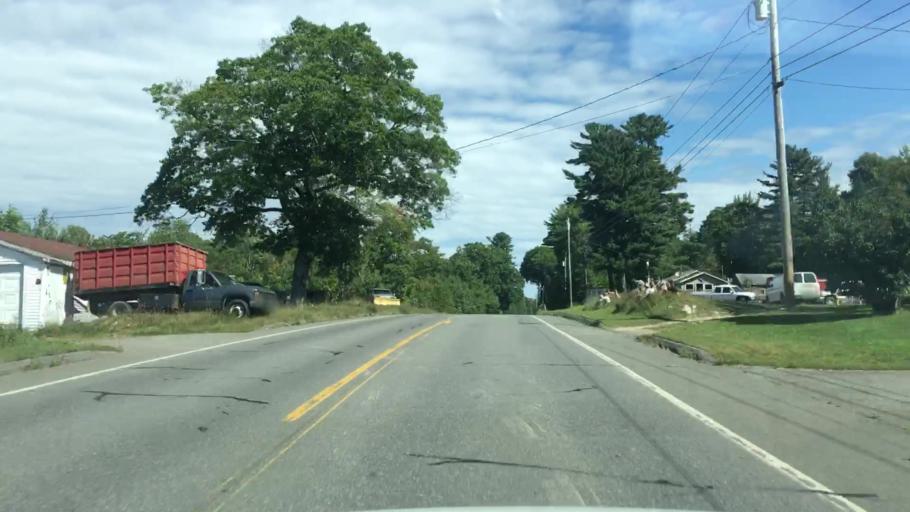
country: US
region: Maine
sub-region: Penobscot County
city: Garland
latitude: 45.0824
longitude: -69.2287
